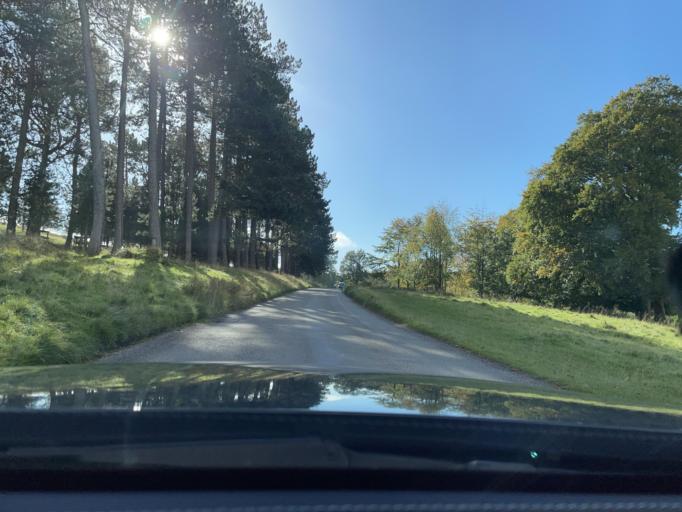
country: GB
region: England
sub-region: Cheshire East
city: Disley
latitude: 53.3448
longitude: -2.0567
